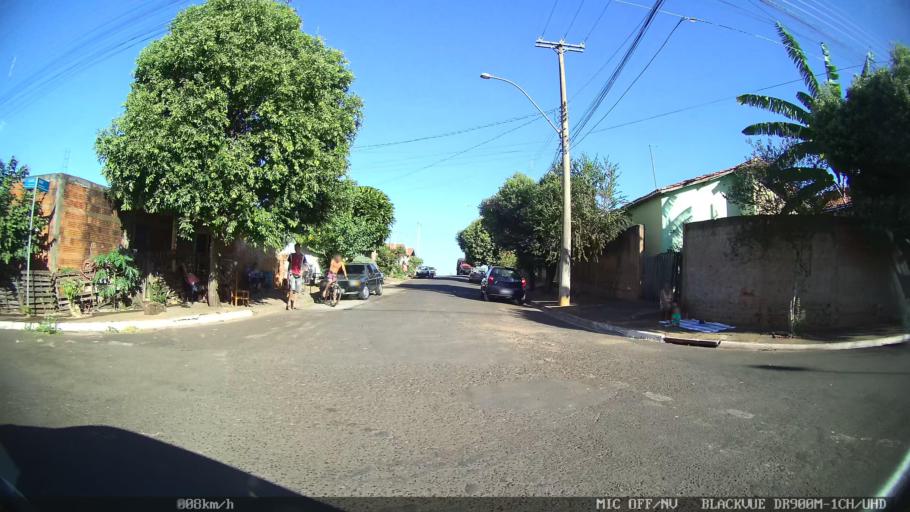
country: BR
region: Sao Paulo
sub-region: Olimpia
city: Olimpia
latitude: -20.7241
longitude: -48.8894
